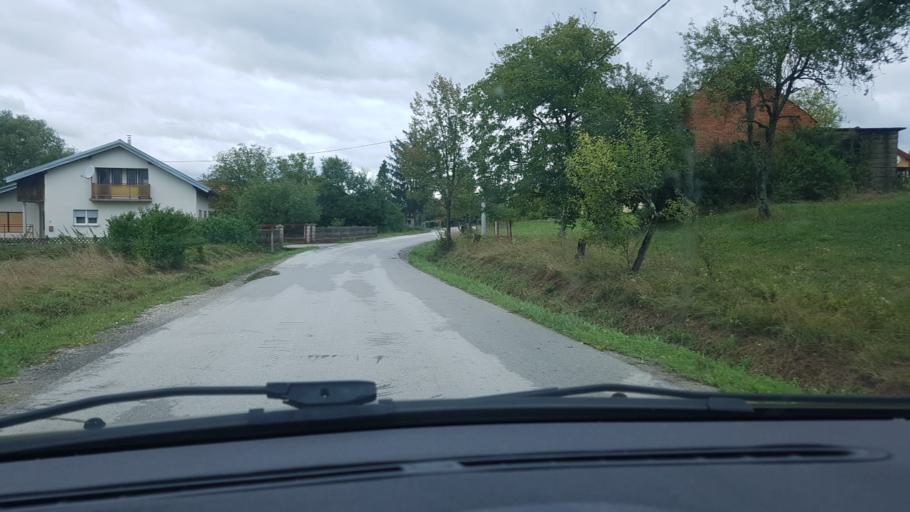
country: HR
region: Karlovacka
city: Ozalj
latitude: 45.5765
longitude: 15.5449
